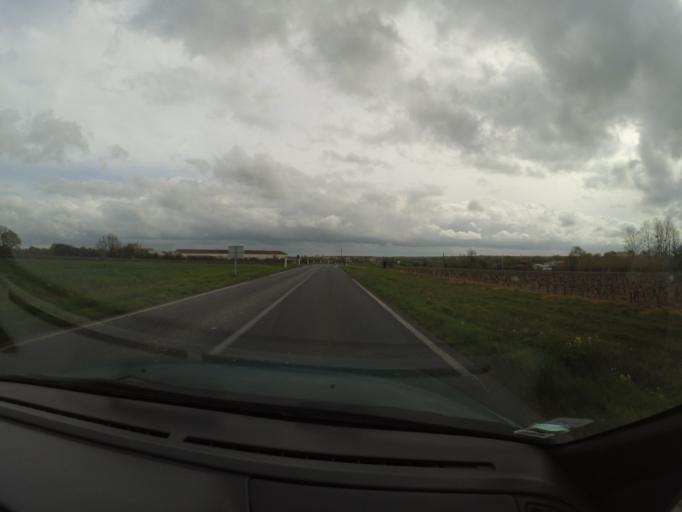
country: FR
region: Pays de la Loire
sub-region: Departement de Maine-et-Loire
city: Lire
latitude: 47.3103
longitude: -1.1614
